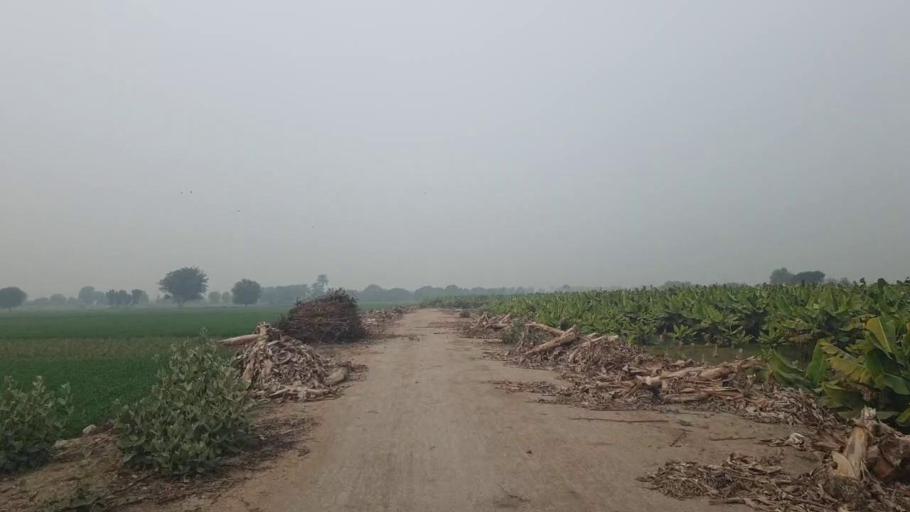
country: PK
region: Sindh
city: Tando Adam
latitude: 25.7215
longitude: 68.6296
